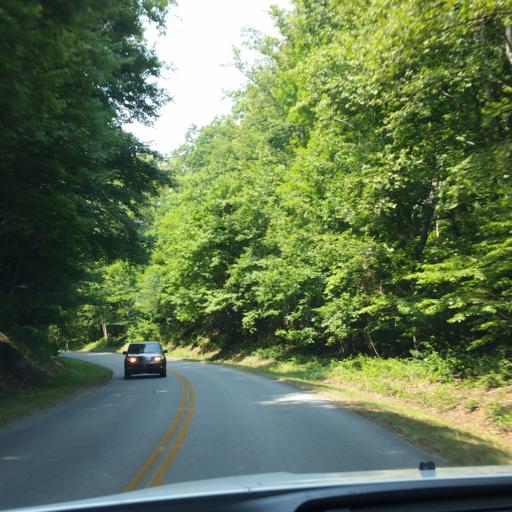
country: US
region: North Carolina
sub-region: Buncombe County
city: Biltmore Forest
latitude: 35.5370
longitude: -82.5036
